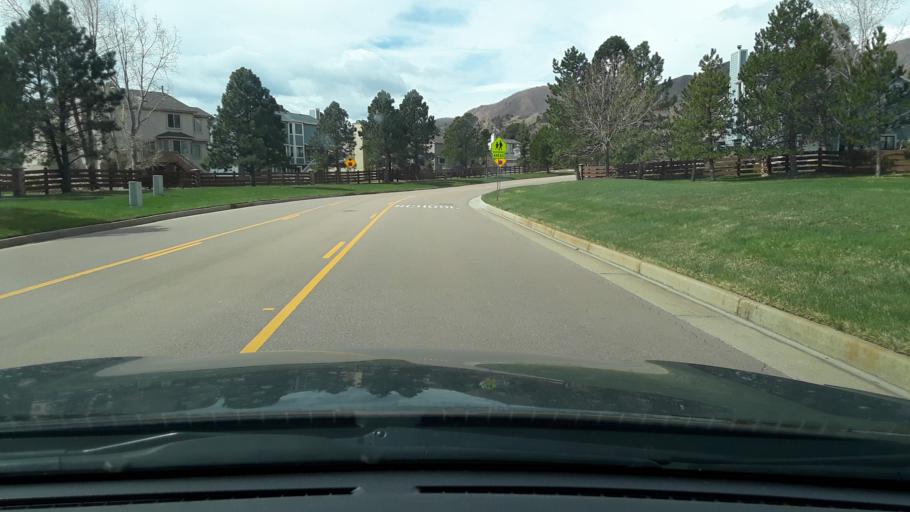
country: US
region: Colorado
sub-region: El Paso County
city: Air Force Academy
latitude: 38.9499
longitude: -104.8660
